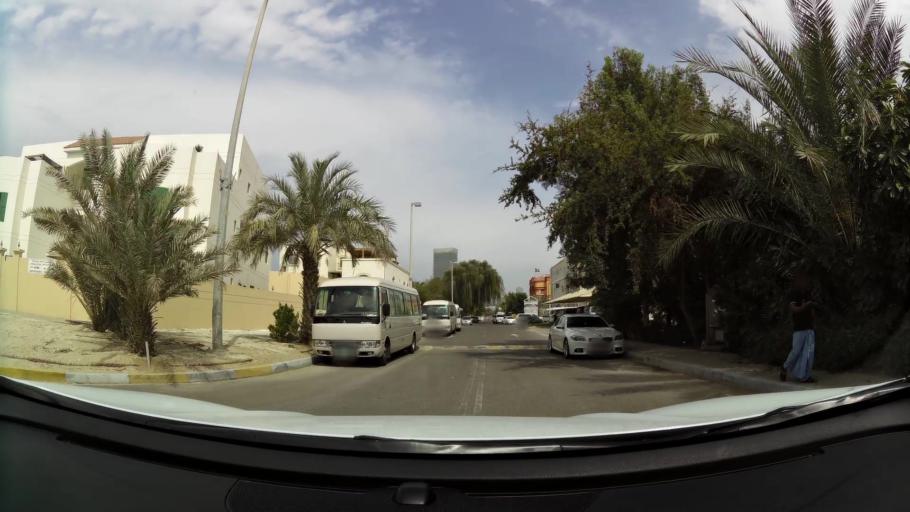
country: AE
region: Abu Dhabi
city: Abu Dhabi
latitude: 24.4586
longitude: 54.3341
